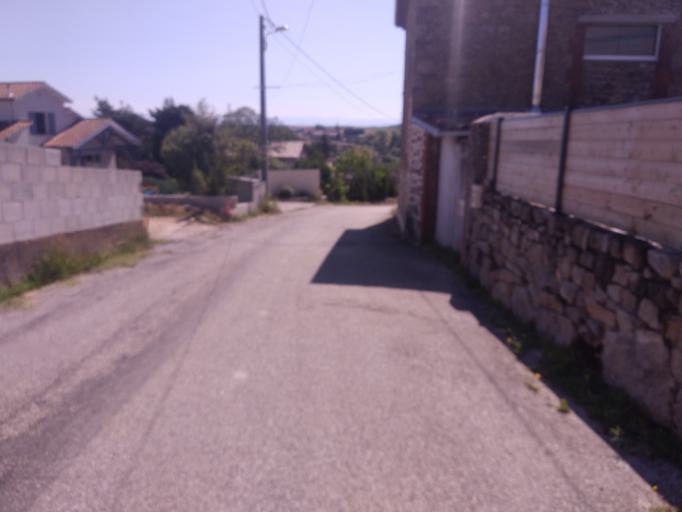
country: FR
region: Rhone-Alpes
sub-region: Departement de l'Ardeche
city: Vernosc-les-Annonay
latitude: 45.1872
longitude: 4.7384
